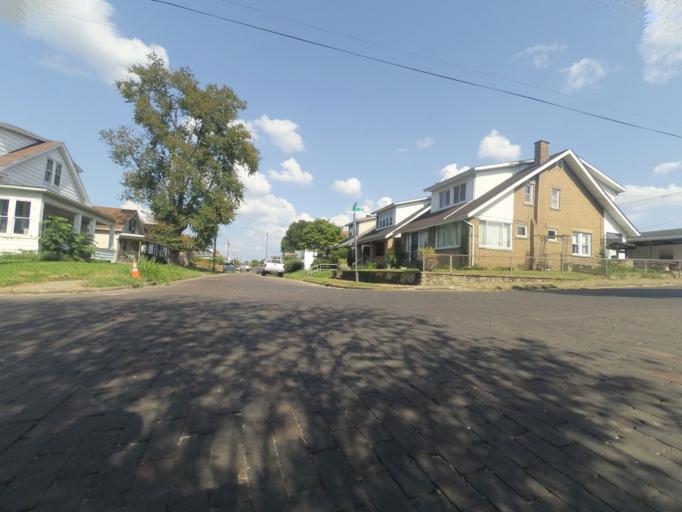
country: US
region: West Virginia
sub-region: Cabell County
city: Huntington
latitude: 38.4148
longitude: -82.4634
